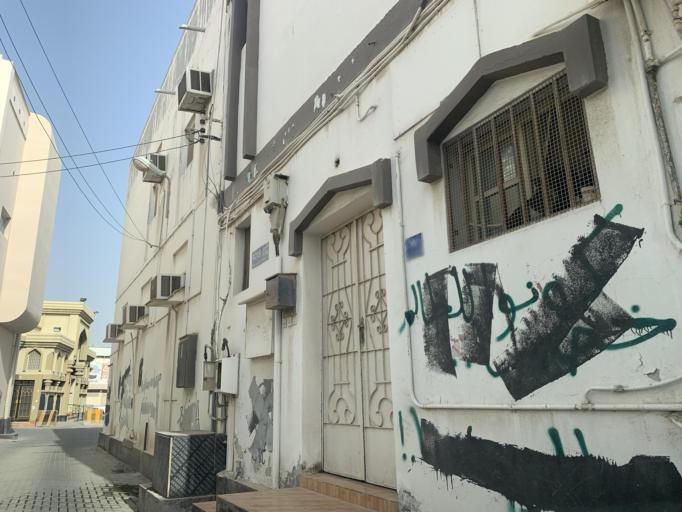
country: BH
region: Northern
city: Madinat `Isa
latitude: 26.1619
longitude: 50.5167
